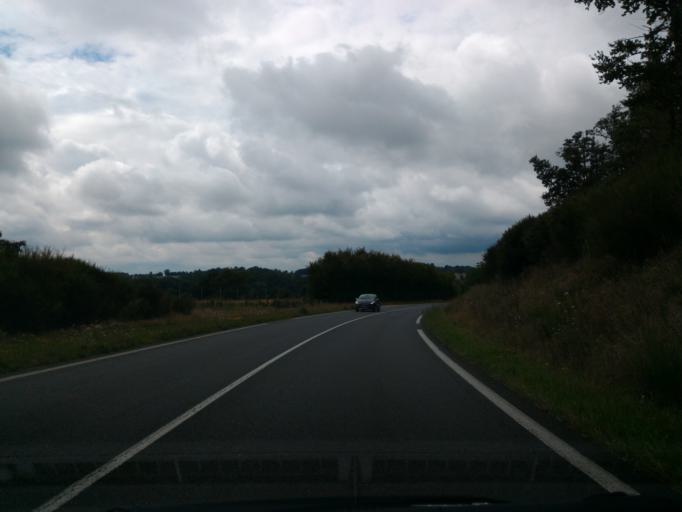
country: FR
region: Poitou-Charentes
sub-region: Departement de la Charente
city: Chabanais
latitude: 45.8794
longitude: 0.7493
